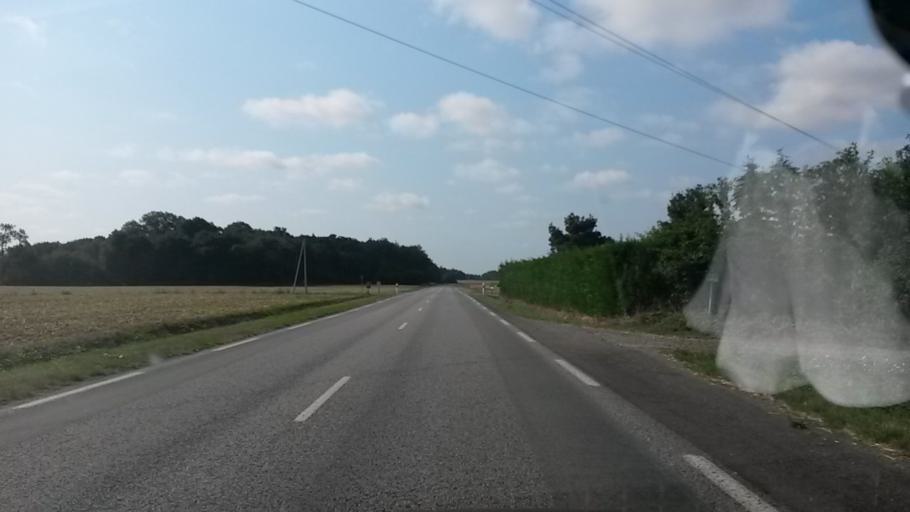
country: FR
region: Haute-Normandie
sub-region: Departement de l'Eure
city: Tillieres-sur-Avre
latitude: 48.8194
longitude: 1.0063
